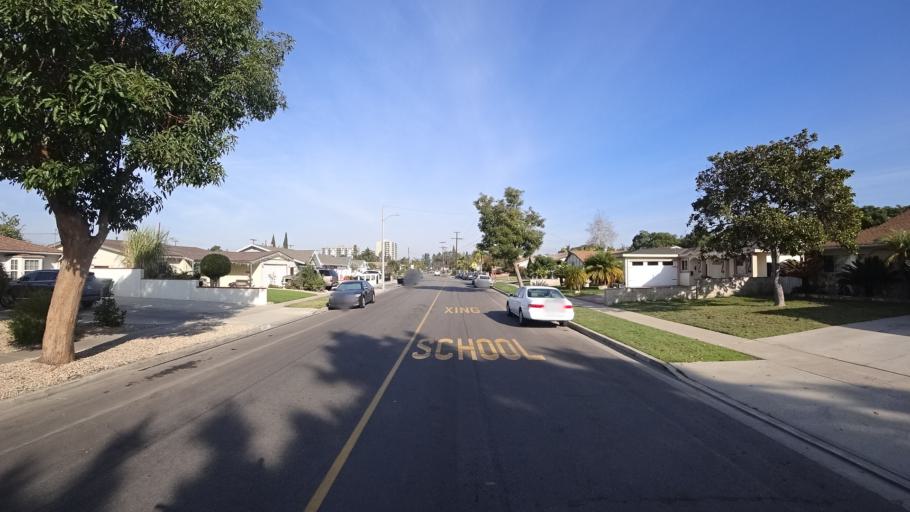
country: US
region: California
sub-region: Orange County
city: Santa Ana
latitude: 33.7705
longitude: -117.8948
